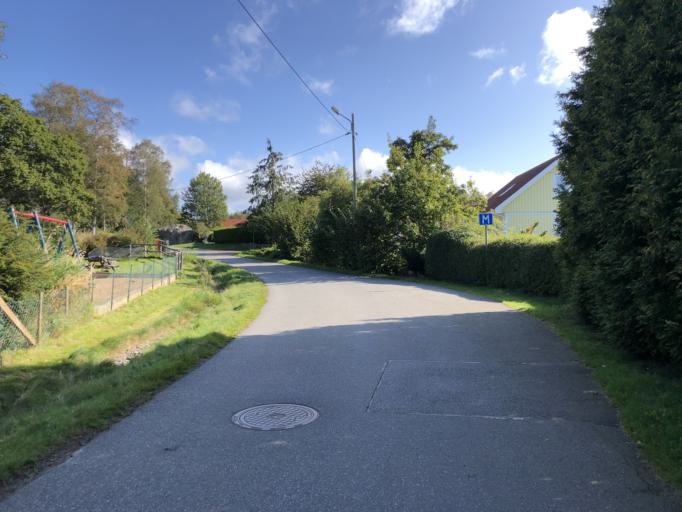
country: SE
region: Vaestra Goetaland
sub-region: Goteborg
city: Torslanda
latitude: 57.7462
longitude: 11.8196
